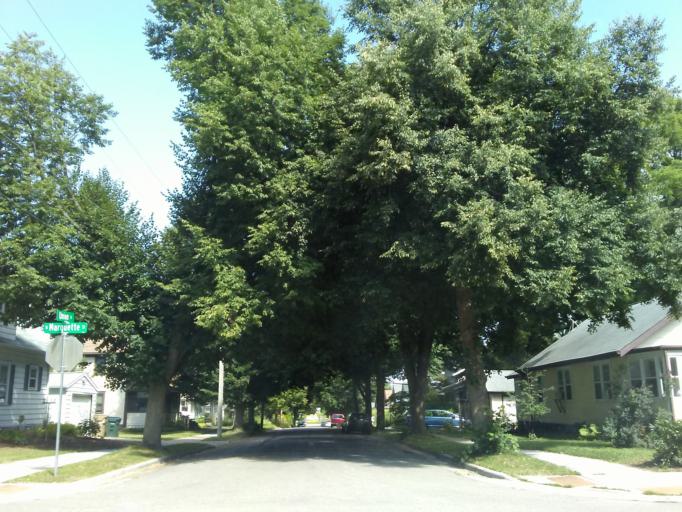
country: US
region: Wisconsin
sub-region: Dane County
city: Monona
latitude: 43.1007
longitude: -89.3417
